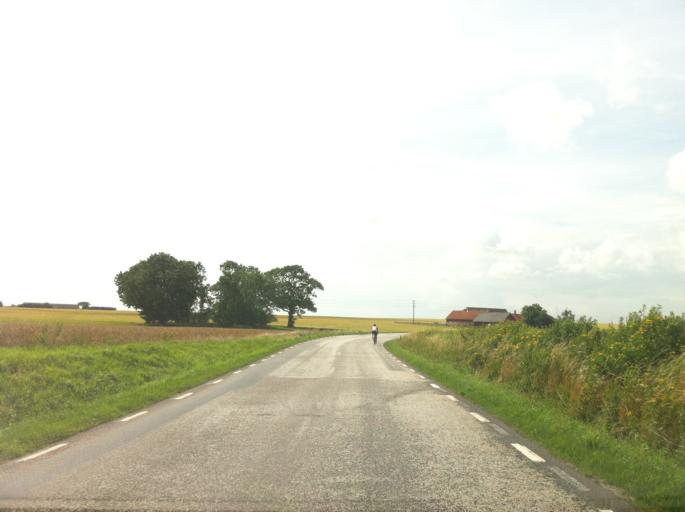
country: SE
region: Skane
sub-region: Lunds Kommun
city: Genarp
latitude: 55.5047
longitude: 13.4008
